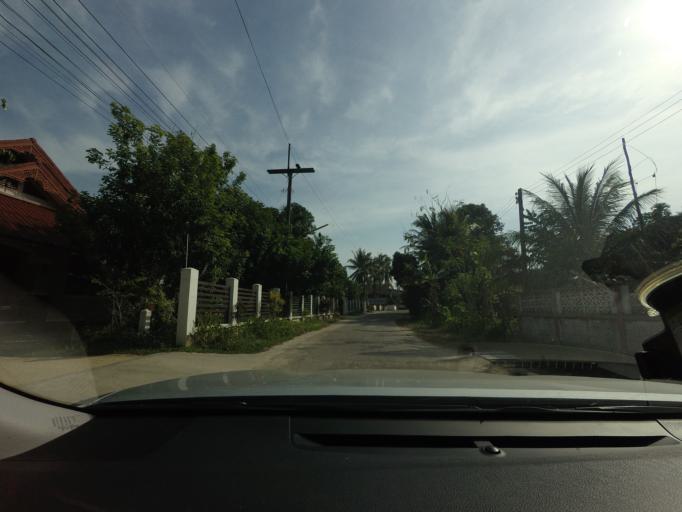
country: TH
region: Narathiwat
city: Ra-ngae
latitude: 6.3102
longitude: 101.7784
